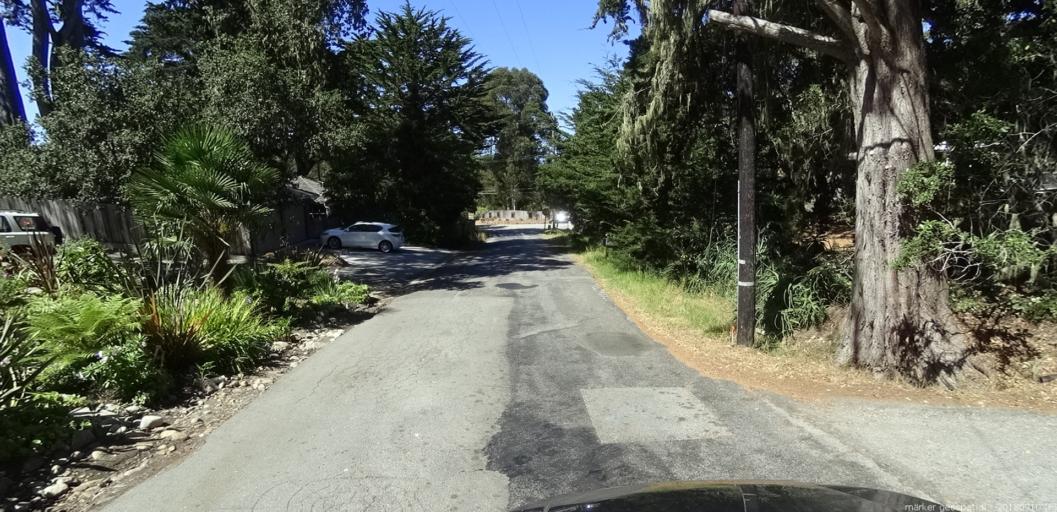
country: US
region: California
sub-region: Monterey County
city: Carmel-by-the-Sea
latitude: 36.5057
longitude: -121.9352
